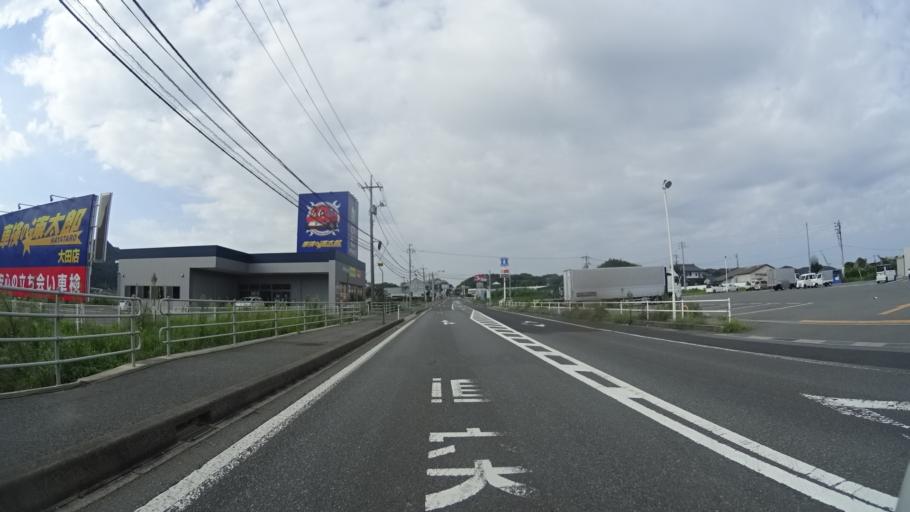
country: JP
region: Shimane
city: Odacho-oda
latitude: 35.2236
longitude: 132.5157
